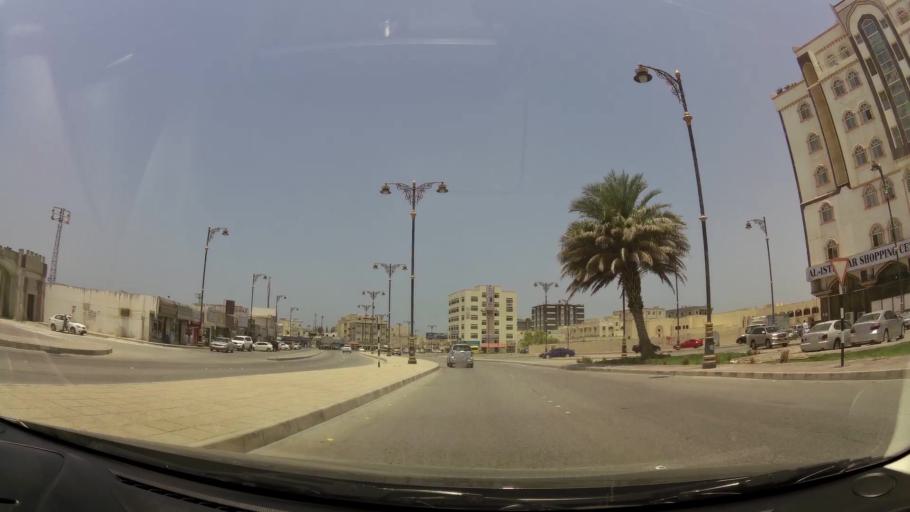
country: OM
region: Zufar
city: Salalah
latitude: 17.0188
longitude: 54.1106
